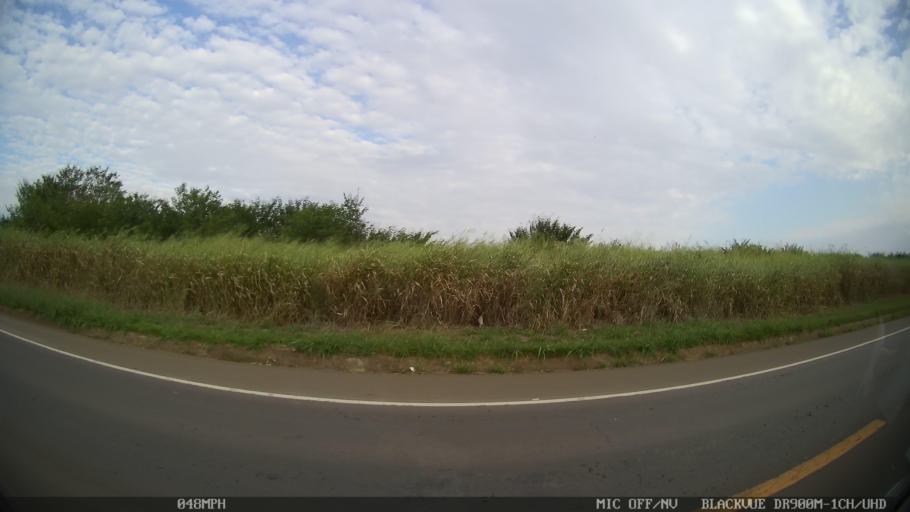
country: BR
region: Sao Paulo
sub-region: Cosmopolis
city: Cosmopolis
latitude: -22.6152
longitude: -47.2424
